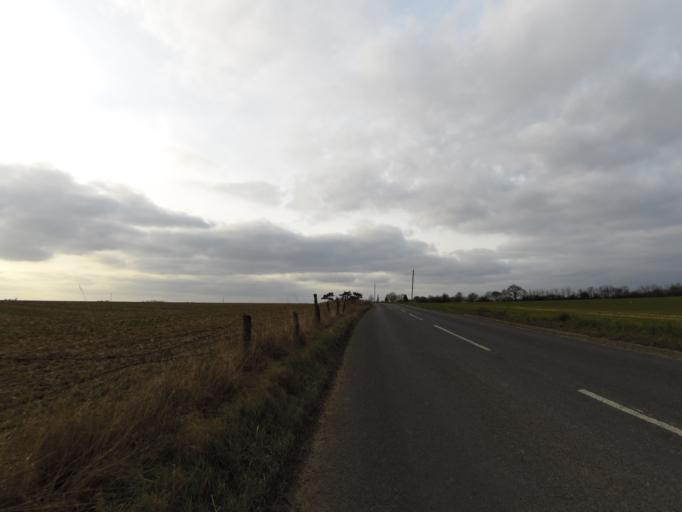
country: GB
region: England
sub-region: Suffolk
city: Ipswich
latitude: 52.0966
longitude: 1.1549
